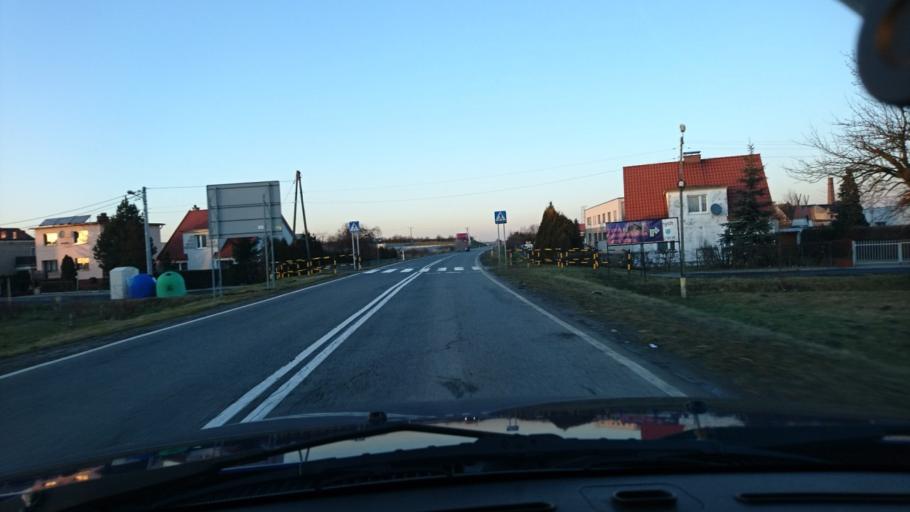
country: PL
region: Silesian Voivodeship
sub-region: Powiat gliwicki
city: Wielowies
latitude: 50.5043
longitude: 18.6046
